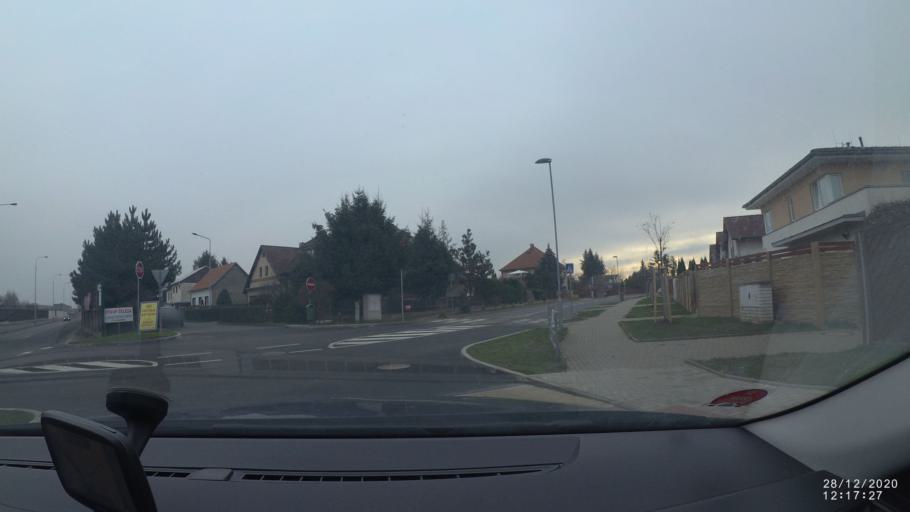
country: CZ
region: Central Bohemia
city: Brandys nad Labem-Stara Boleslav
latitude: 50.1766
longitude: 14.6539
